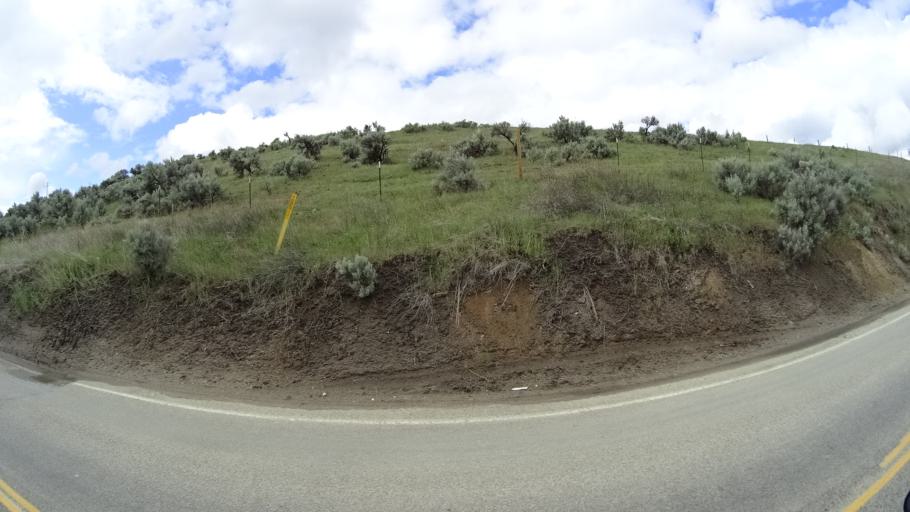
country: US
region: Idaho
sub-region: Ada County
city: Eagle
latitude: 43.7300
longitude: -116.2843
